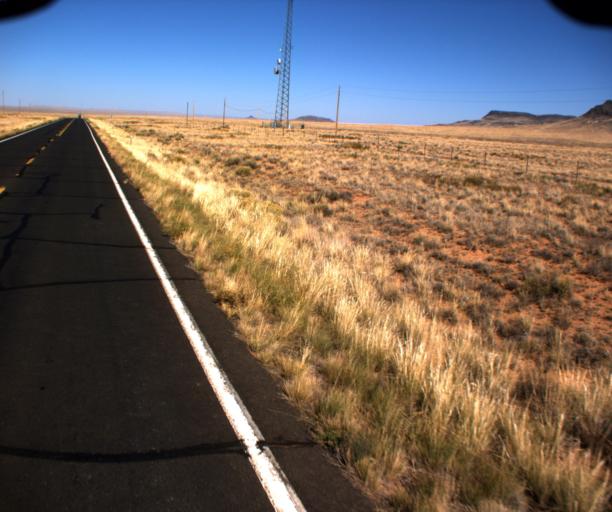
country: US
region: Arizona
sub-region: Navajo County
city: Dilkon
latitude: 35.5144
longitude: -110.4396
